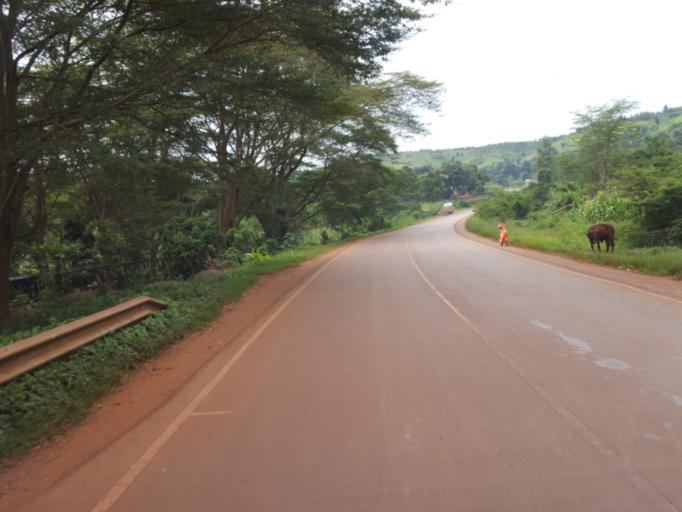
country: UG
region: Central Region
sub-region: Mityana District
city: Mityana
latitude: 0.6307
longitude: 32.1152
